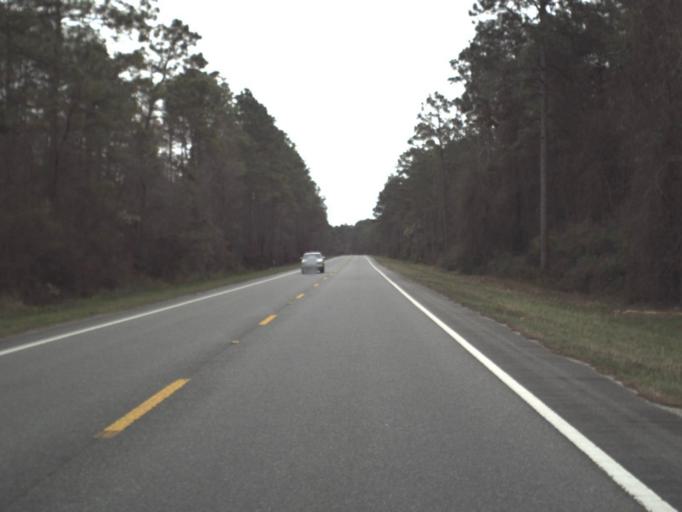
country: US
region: Florida
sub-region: Gadsden County
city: Midway
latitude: 30.3619
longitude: -84.5356
